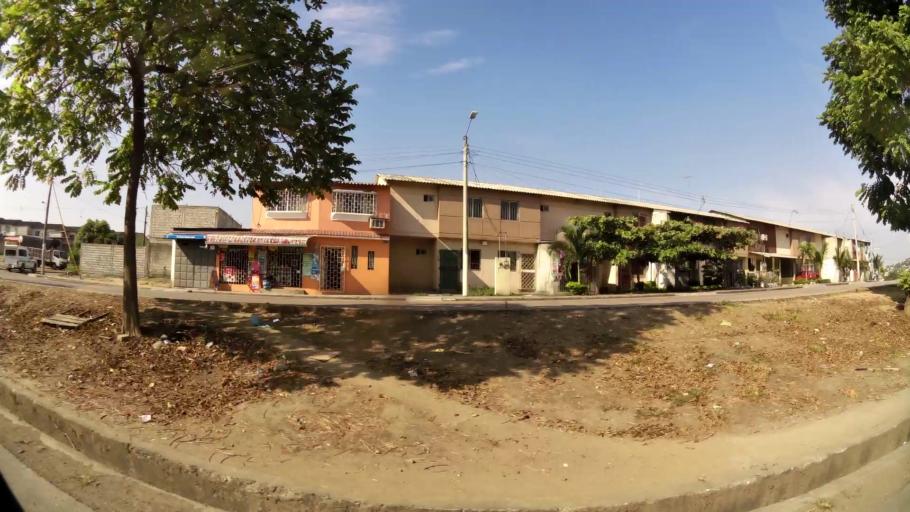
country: EC
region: Guayas
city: Eloy Alfaro
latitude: -2.0769
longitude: -79.9209
